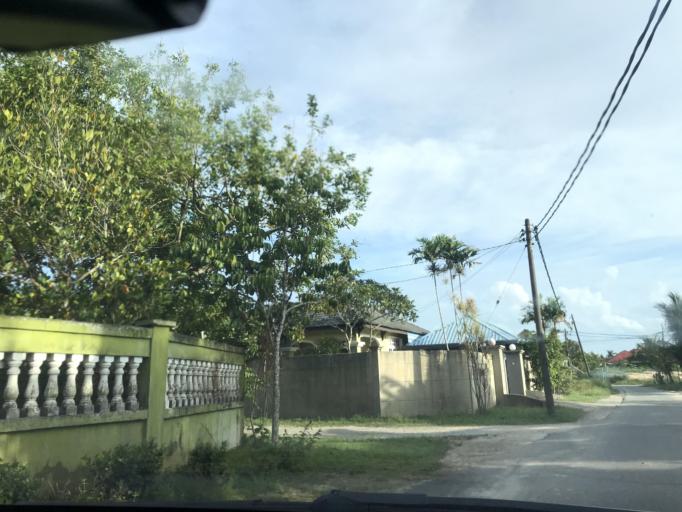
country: MY
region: Kelantan
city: Kota Bharu
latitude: 6.1288
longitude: 102.2212
